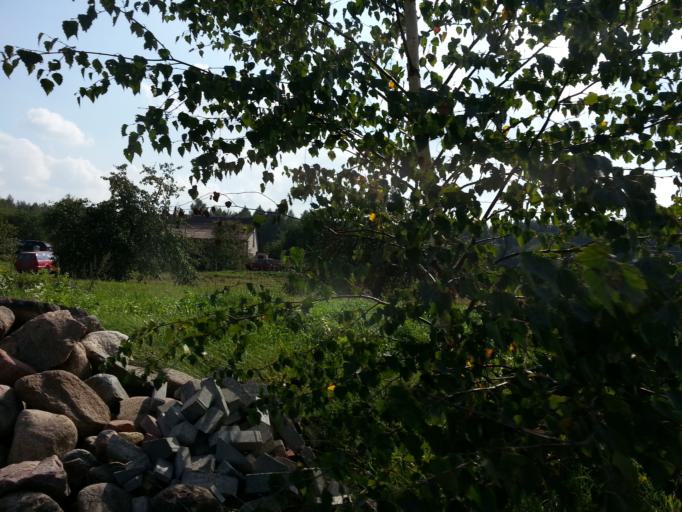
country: LT
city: Grigiskes
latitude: 54.7616
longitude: 25.0746
